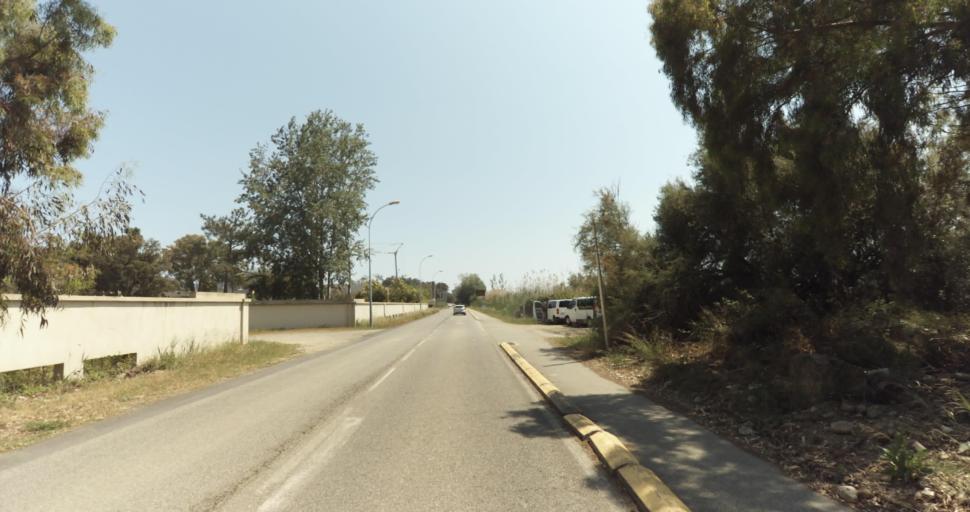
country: FR
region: Corsica
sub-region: Departement de la Haute-Corse
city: Biguglia
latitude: 42.6114
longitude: 9.4821
